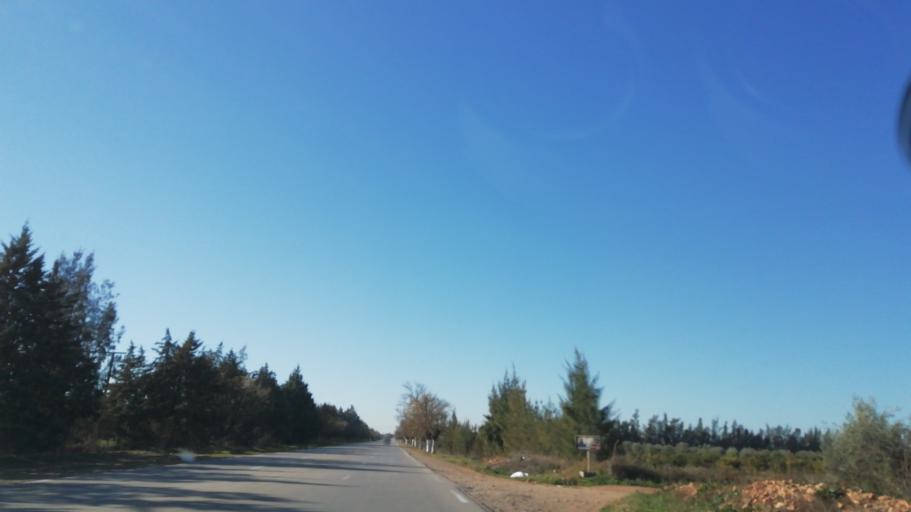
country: MA
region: Oriental
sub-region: Oujda-Angad
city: Oujda
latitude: 34.8151
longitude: -1.8085
